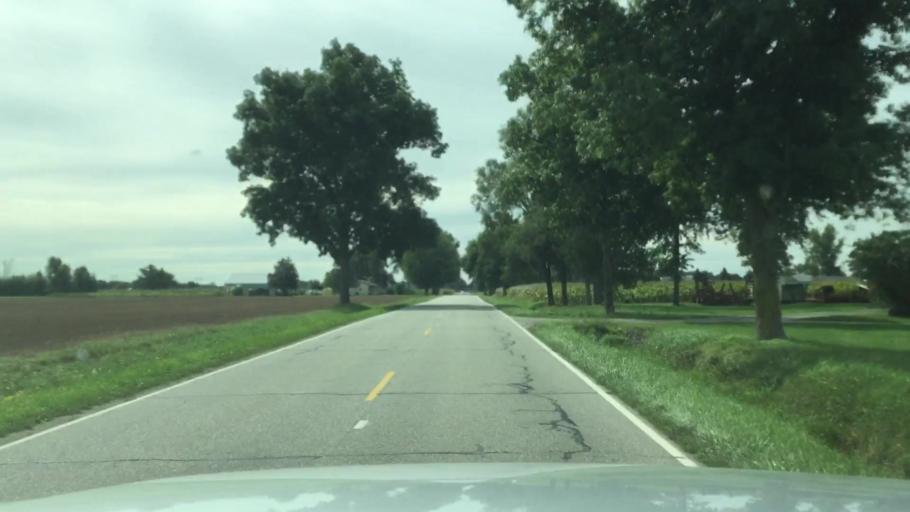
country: US
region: Michigan
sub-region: Genesee County
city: Montrose
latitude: 43.1269
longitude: -83.9880
